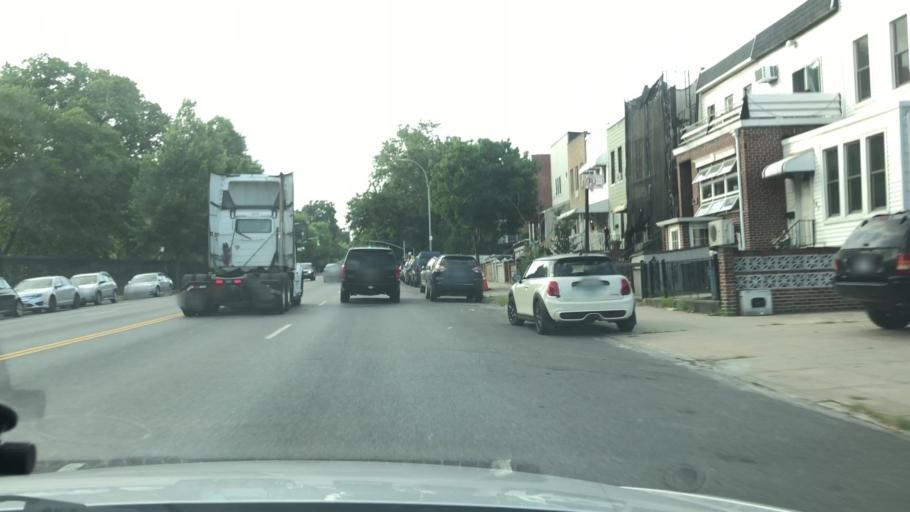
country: US
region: New York
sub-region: Kings County
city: Brooklyn
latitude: 40.6503
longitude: -73.9809
